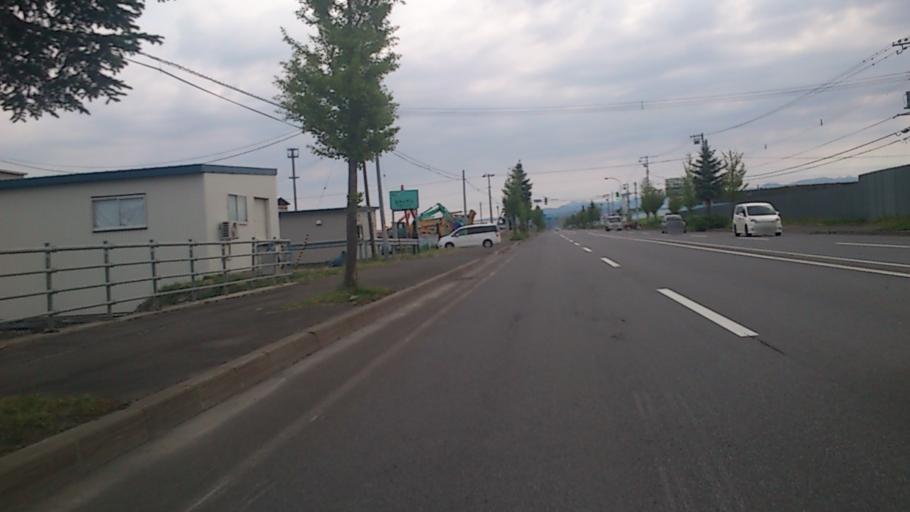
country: JP
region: Hokkaido
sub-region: Asahikawa-shi
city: Asahikawa
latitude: 43.8406
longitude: 142.4819
